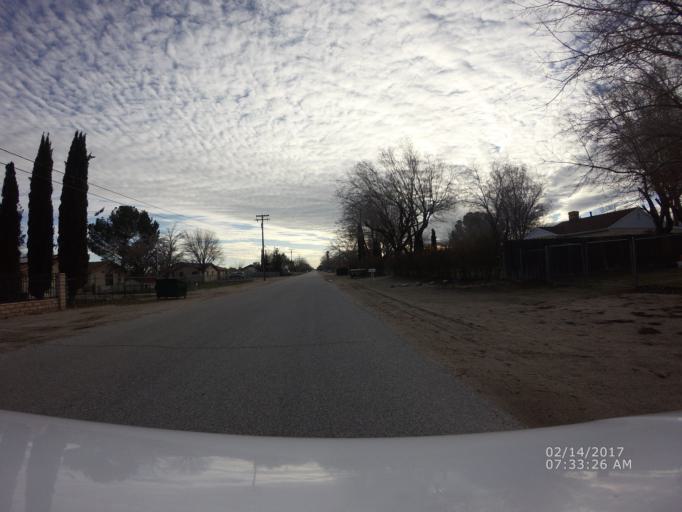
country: US
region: California
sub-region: Los Angeles County
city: Littlerock
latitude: 34.5466
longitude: -117.9573
